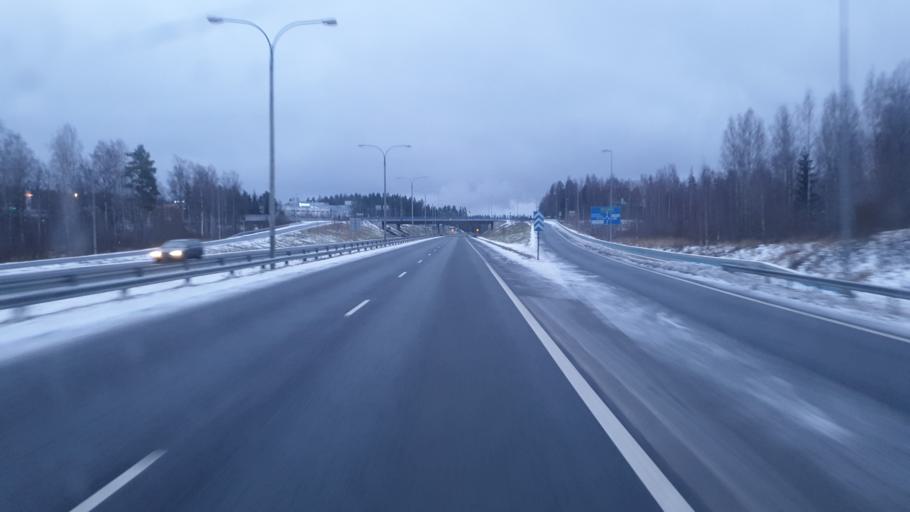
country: FI
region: Northern Savo
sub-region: Kuopio
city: Kuopio
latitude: 62.9757
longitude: 27.7055
